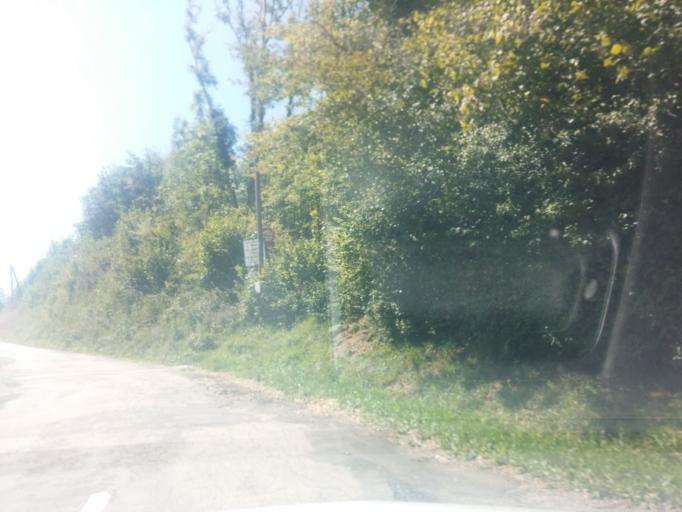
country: FR
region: Franche-Comte
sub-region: Departement du Jura
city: Saint-Lupicin
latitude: 46.4119
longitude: 5.7949
